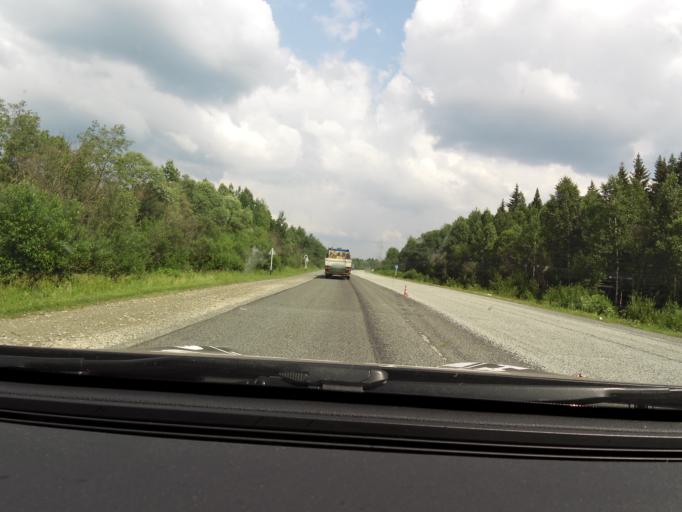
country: RU
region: Sverdlovsk
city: Ufimskiy
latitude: 56.7708
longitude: 58.1009
